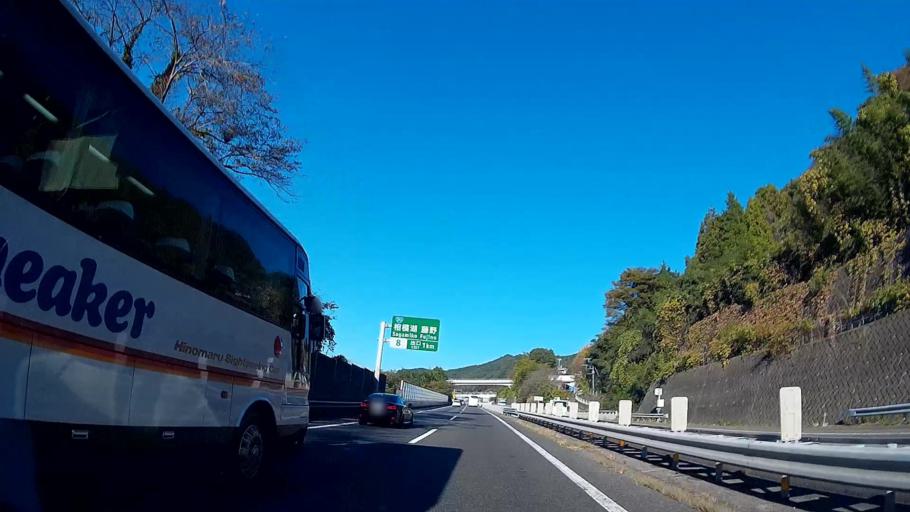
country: JP
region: Yamanashi
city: Uenohara
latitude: 35.6208
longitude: 139.1797
